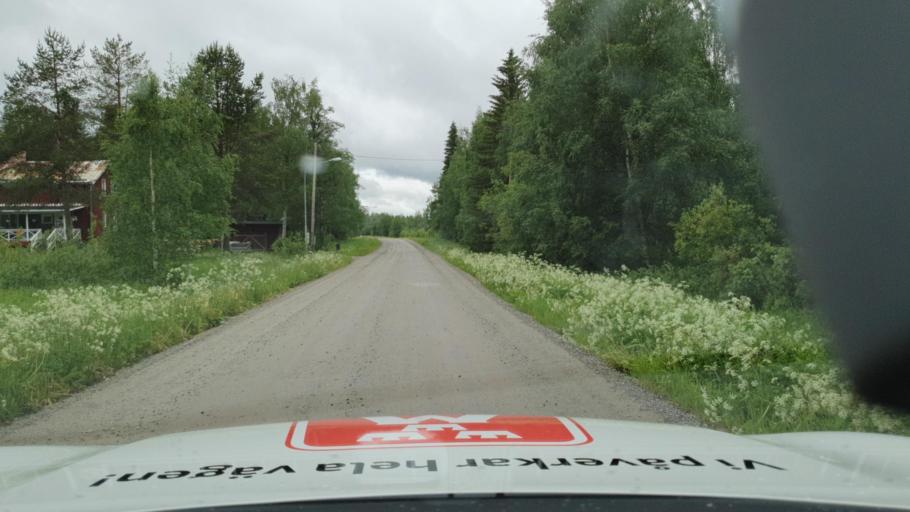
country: SE
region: Vaesterbotten
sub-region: Dorotea Kommun
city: Dorotea
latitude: 64.0909
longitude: 16.6682
